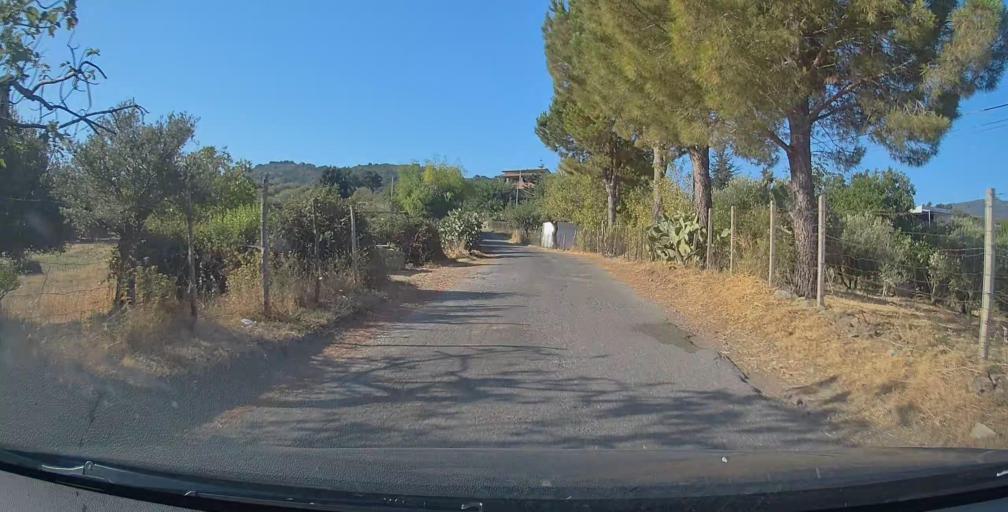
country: IT
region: Sicily
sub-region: Messina
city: San Piero Patti
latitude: 38.0636
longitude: 14.9892
